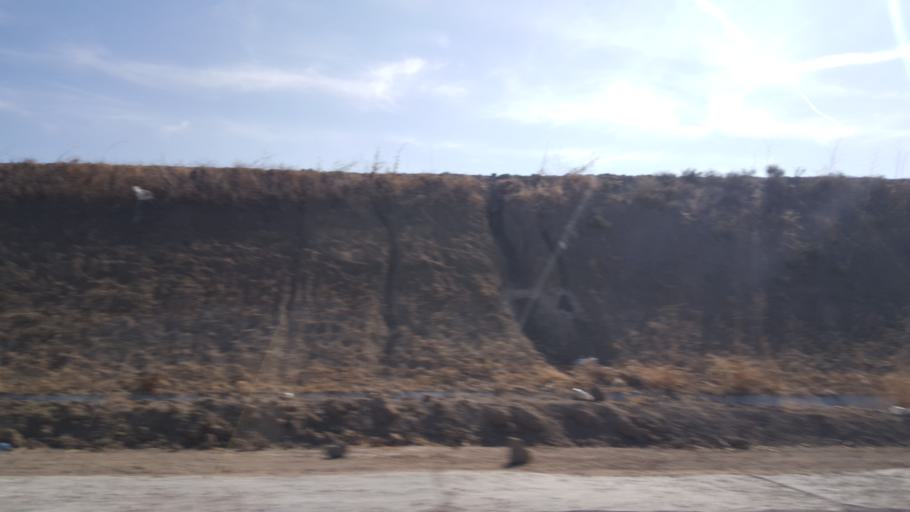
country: TR
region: Ankara
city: Yenice
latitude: 39.3799
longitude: 32.7643
